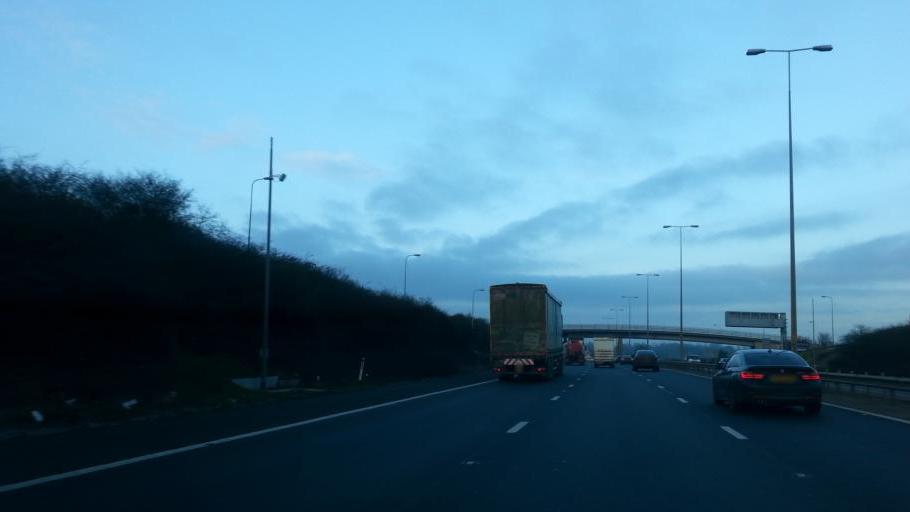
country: GB
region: England
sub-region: Worcestershire
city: Worcester
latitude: 52.1704
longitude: -2.1789
